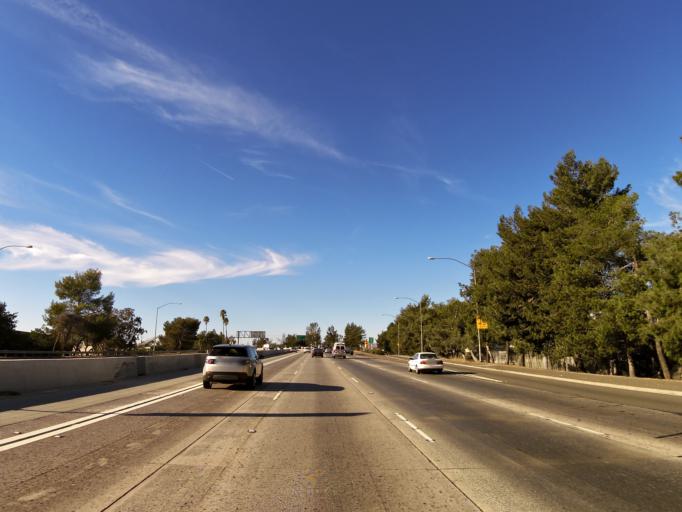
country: US
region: California
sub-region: Los Angeles County
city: North Hollywood
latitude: 34.2240
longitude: -118.3724
